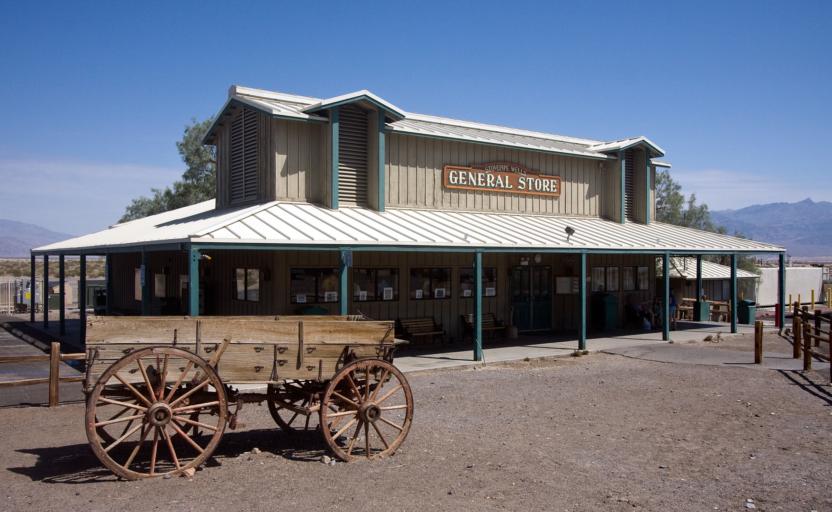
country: US
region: Nevada
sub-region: Nye County
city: Beatty
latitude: 36.6067
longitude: -117.1465
